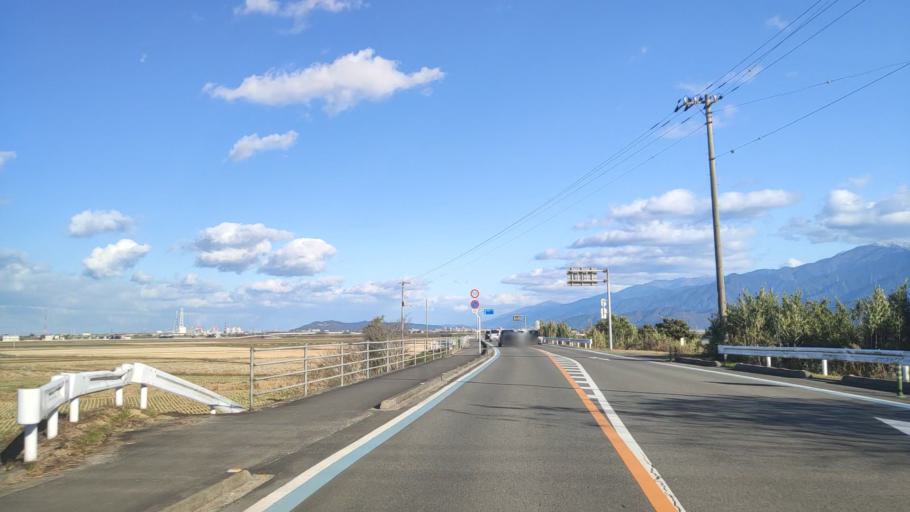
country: JP
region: Ehime
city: Saijo
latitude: 33.9067
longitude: 133.1175
